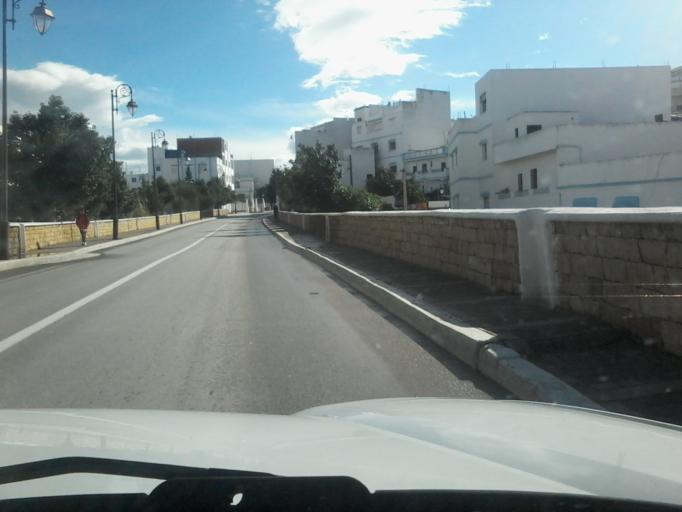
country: MA
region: Tanger-Tetouan
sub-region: Tetouan
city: Martil
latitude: 35.6835
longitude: -5.3285
